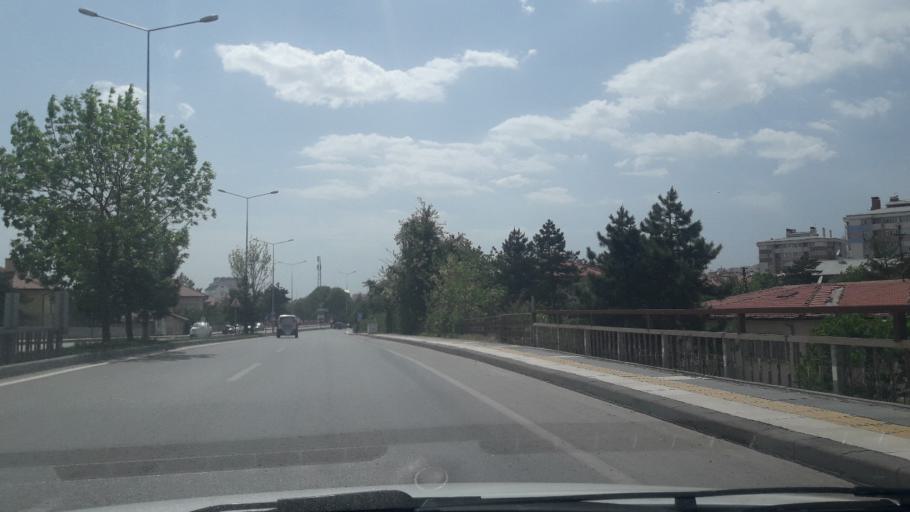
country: TR
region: Sivas
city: Sivas
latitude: 39.7411
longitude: 37.0101
